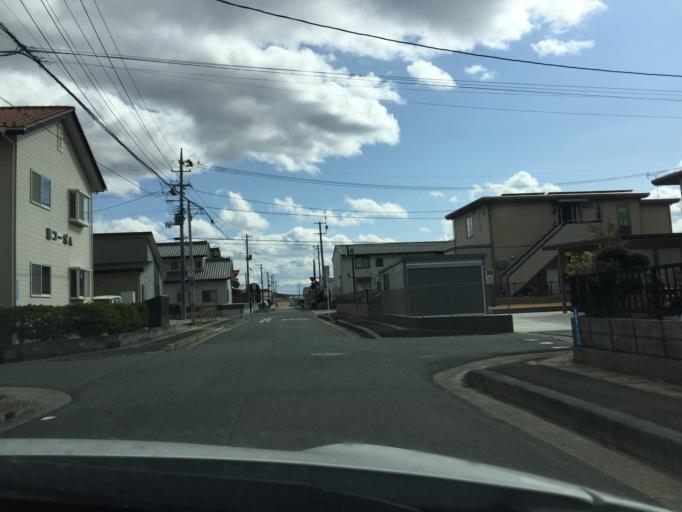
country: JP
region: Miyagi
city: Marumori
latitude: 37.8046
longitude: 140.9341
